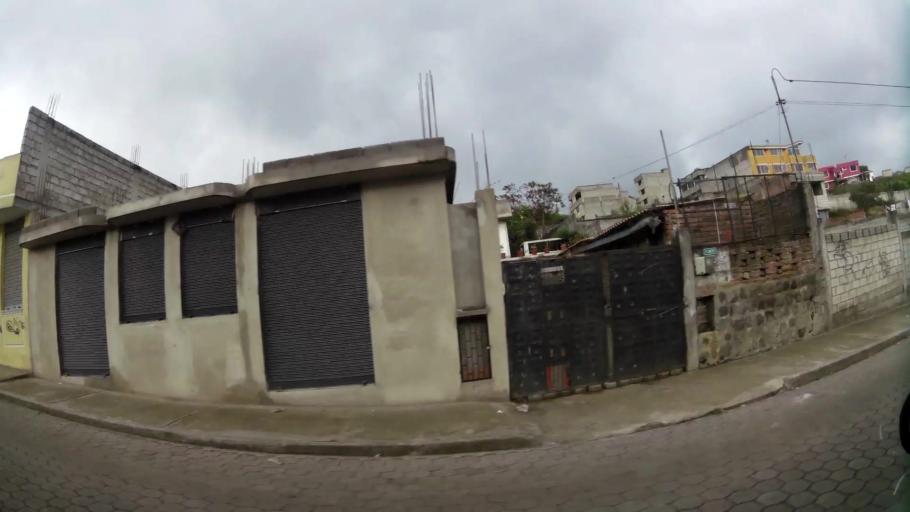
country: EC
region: Pichincha
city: Quito
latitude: -0.3020
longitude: -78.5229
